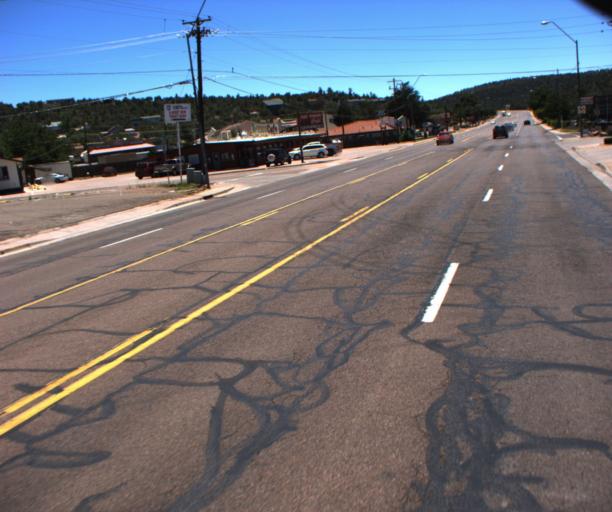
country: US
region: Arizona
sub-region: Gila County
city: Payson
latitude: 34.2289
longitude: -111.3273
